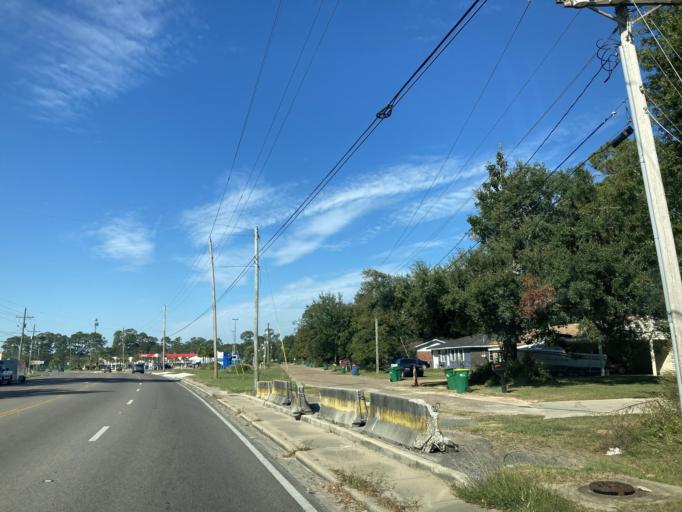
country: US
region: Mississippi
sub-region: Jackson County
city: Saint Martin
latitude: 30.4431
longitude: -88.8705
